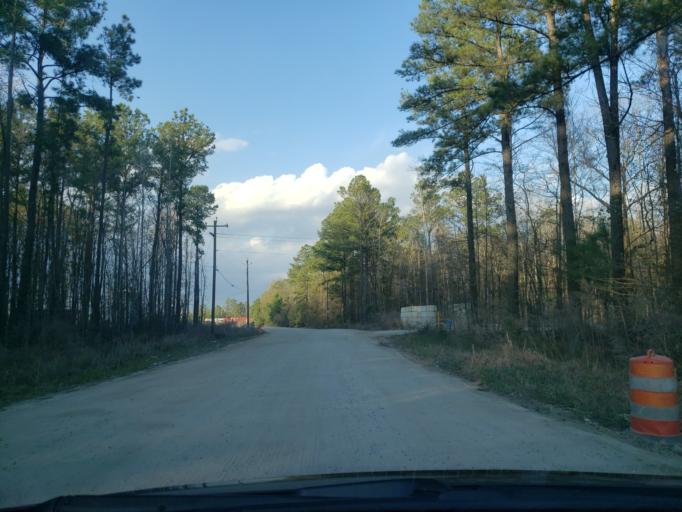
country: US
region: Georgia
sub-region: Chatham County
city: Bloomingdale
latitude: 32.1519
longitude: -81.2852
